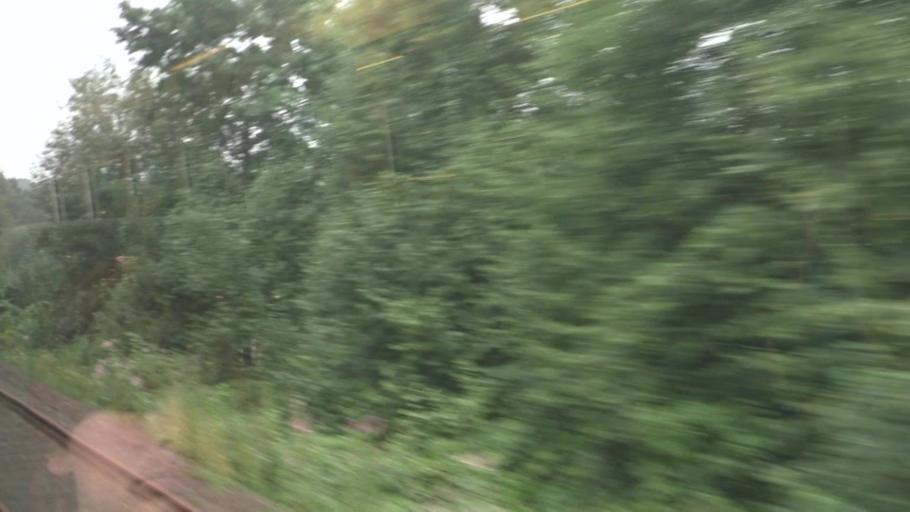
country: DE
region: Saxony
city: Arnsdorf
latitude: 51.1017
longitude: 13.9554
